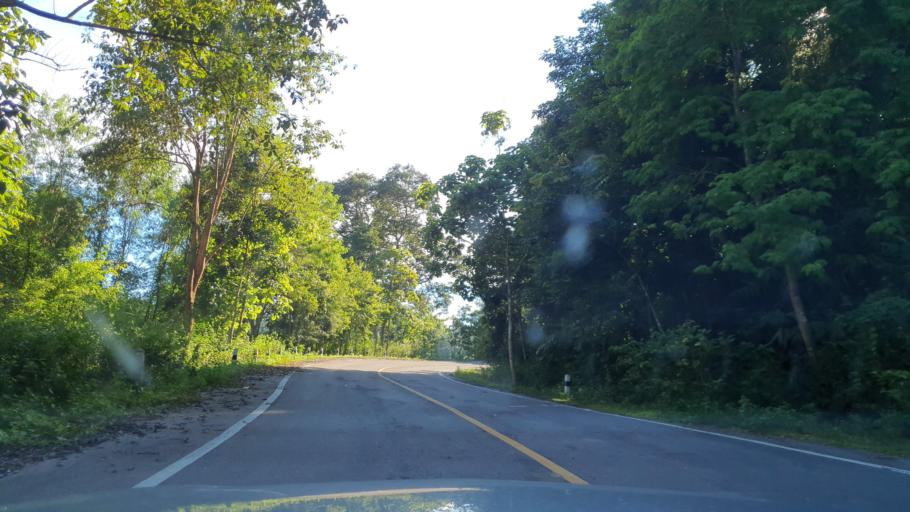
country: TH
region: Chiang Mai
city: Mae On
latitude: 18.7999
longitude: 99.3043
